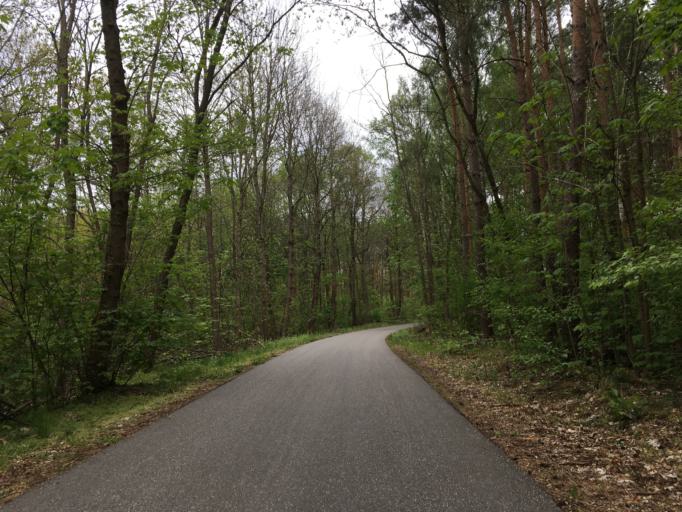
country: DE
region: Brandenburg
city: Bernau bei Berlin
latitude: 52.6950
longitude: 13.5410
